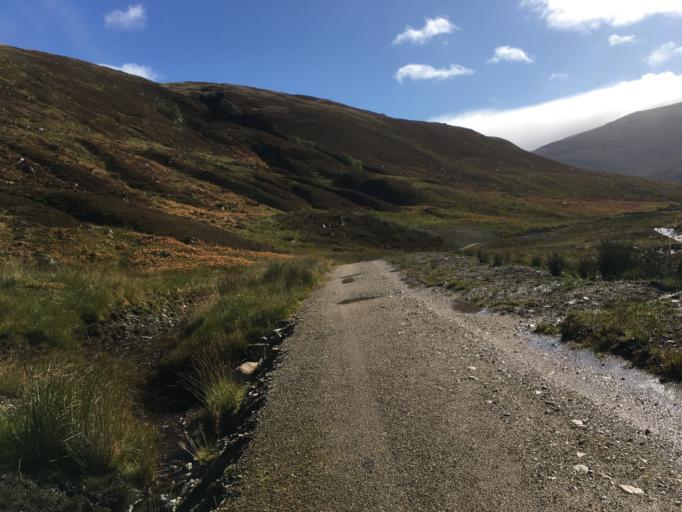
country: GB
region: Scotland
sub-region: Highland
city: Spean Bridge
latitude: 57.3509
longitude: -4.9849
